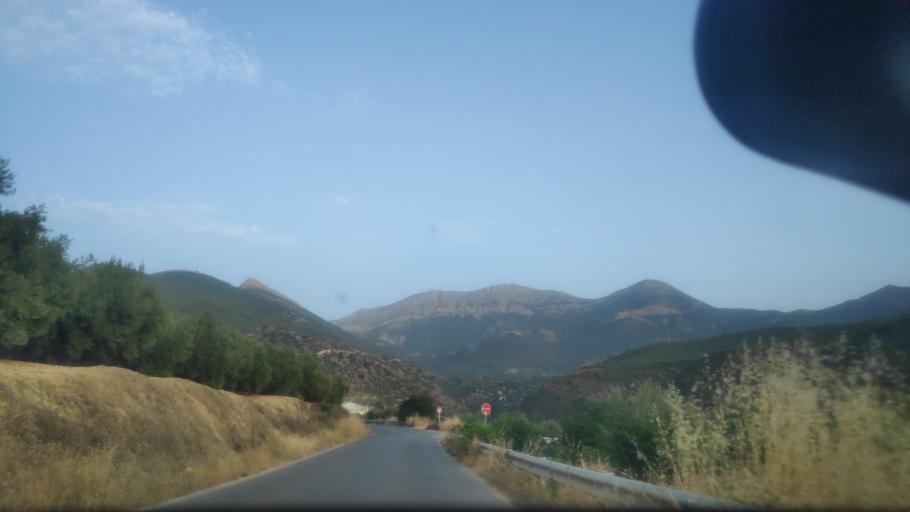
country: ES
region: Andalusia
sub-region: Provincia de Jaen
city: Torres
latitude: 37.7885
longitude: -3.5162
